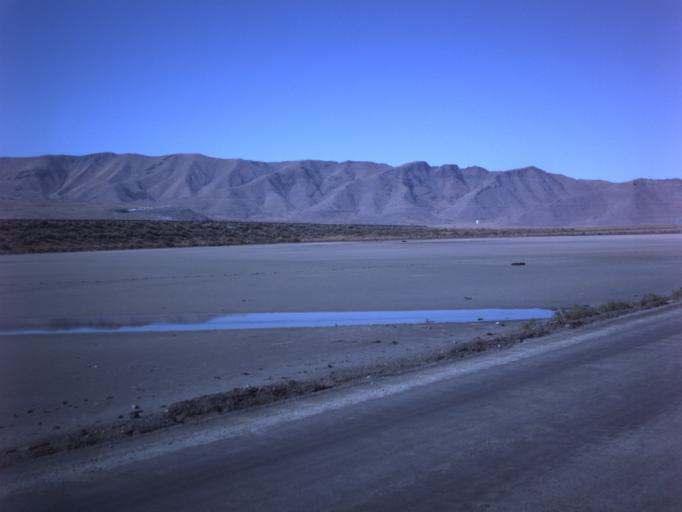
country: US
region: Utah
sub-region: Tooele County
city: Grantsville
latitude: 40.7116
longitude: -112.5282
